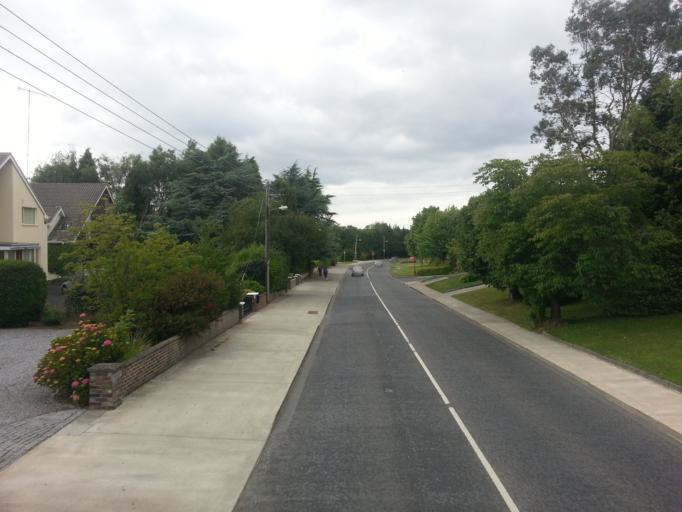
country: IE
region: Leinster
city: Sandyford
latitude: 53.2542
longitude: -6.2147
